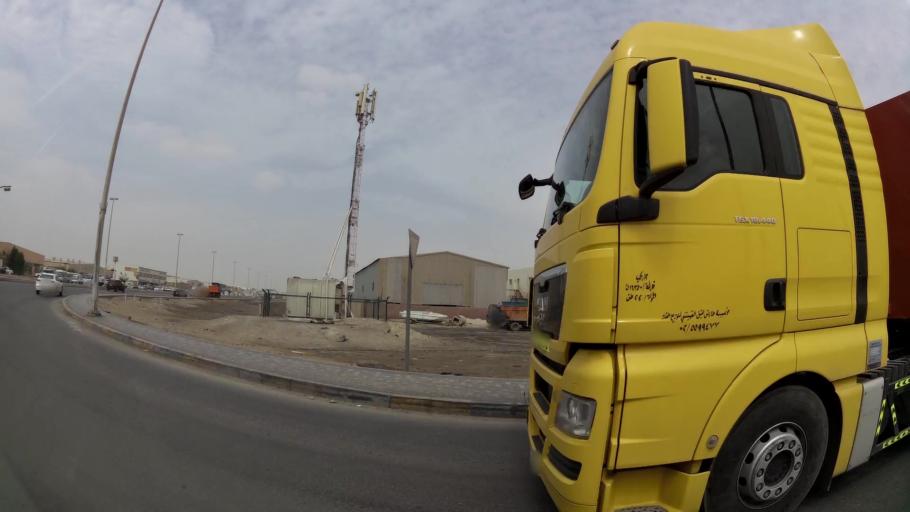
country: AE
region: Abu Dhabi
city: Abu Dhabi
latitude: 24.3549
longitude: 54.5024
